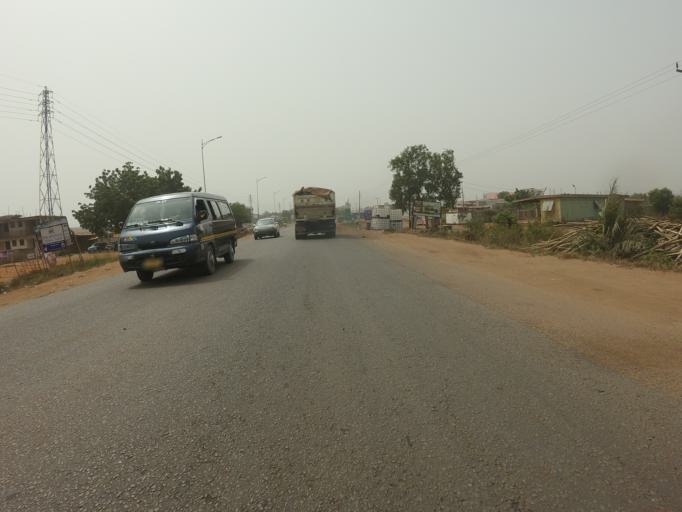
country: GH
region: Greater Accra
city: Tema
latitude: 5.7589
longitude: 0.0503
